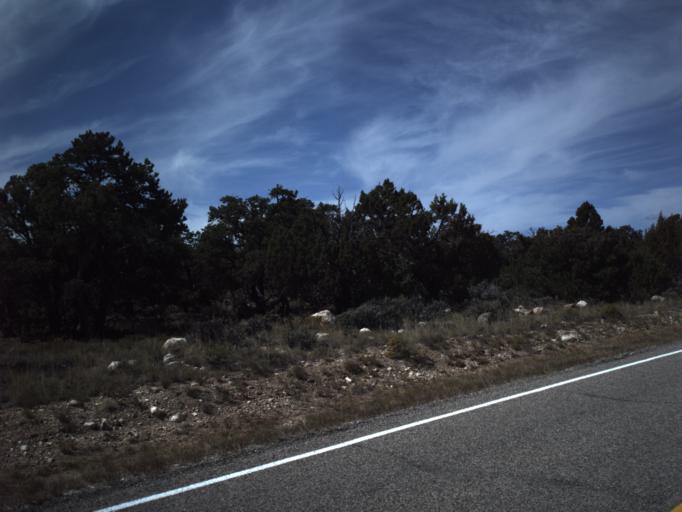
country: US
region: Utah
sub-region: Wayne County
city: Loa
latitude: 37.8791
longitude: -111.4561
